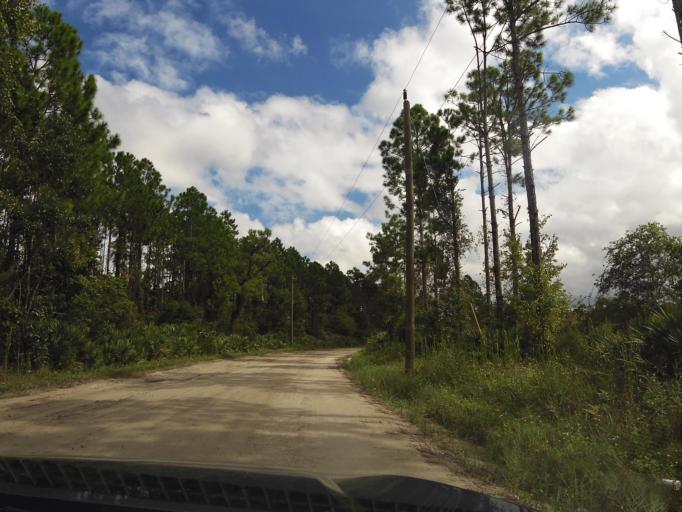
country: US
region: Florida
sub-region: Saint Johns County
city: Palm Valley
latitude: 30.0523
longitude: -81.3926
